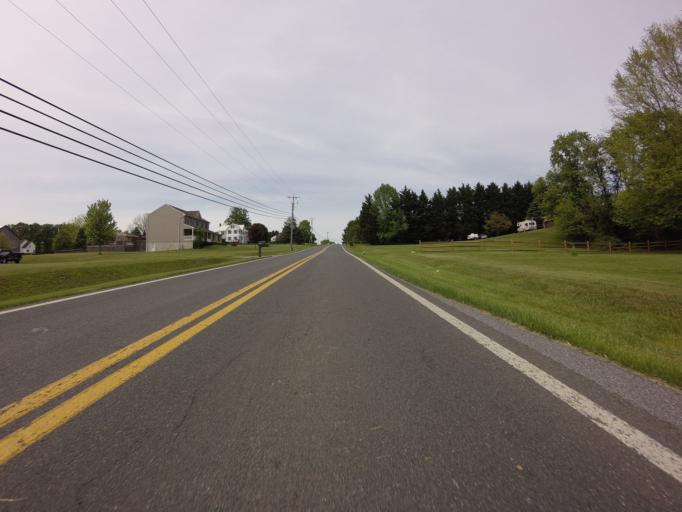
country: US
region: Maryland
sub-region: Carroll County
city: Eldersburg
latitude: 39.4648
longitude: -76.9538
